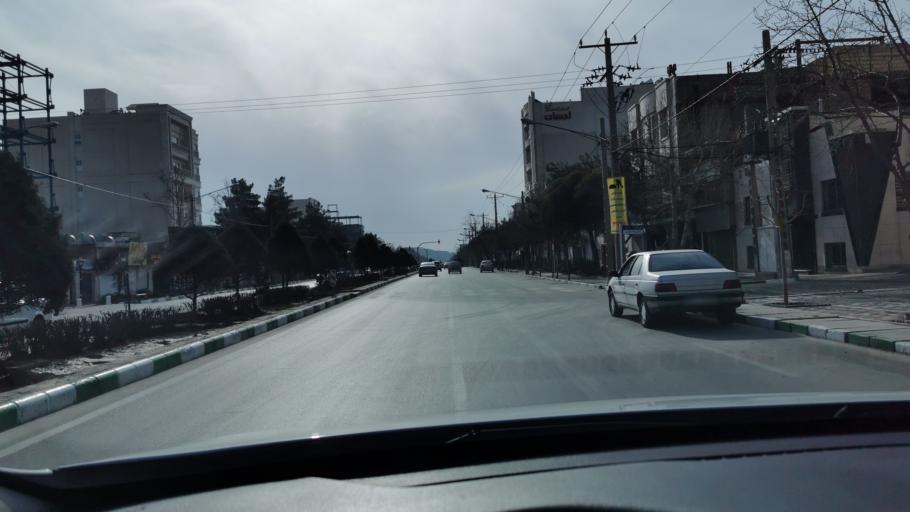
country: IR
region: Razavi Khorasan
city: Mashhad
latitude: 36.2902
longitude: 59.5391
